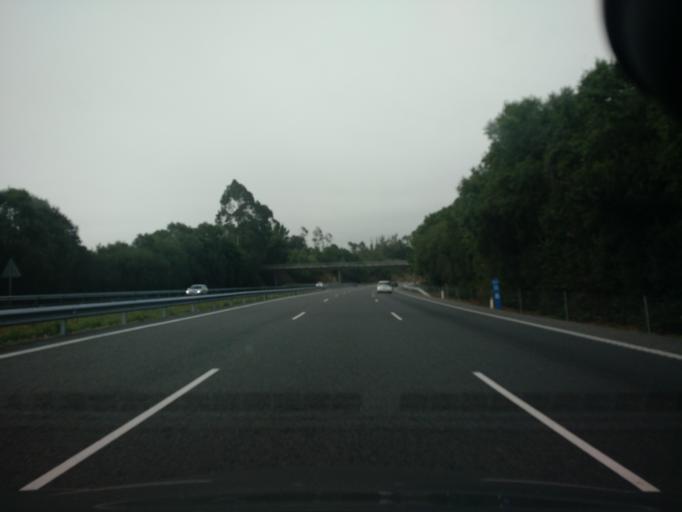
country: ES
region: Galicia
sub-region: Provincia da Coruna
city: Abegondo
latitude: 43.1741
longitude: -8.3133
